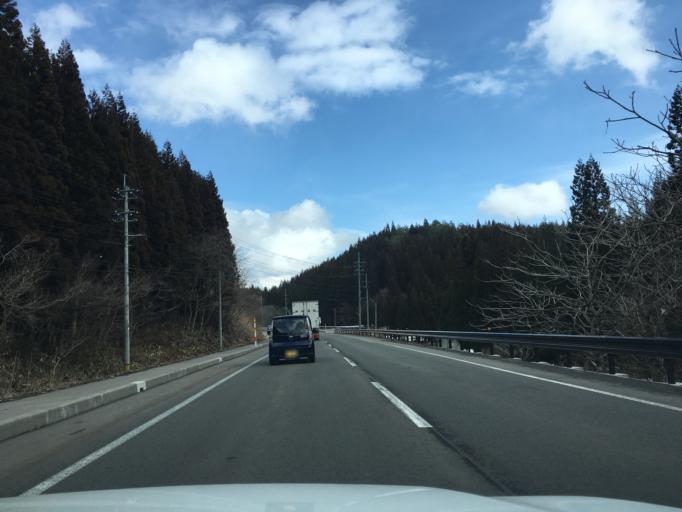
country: JP
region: Akita
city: Takanosu
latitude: 40.0997
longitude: 140.3435
